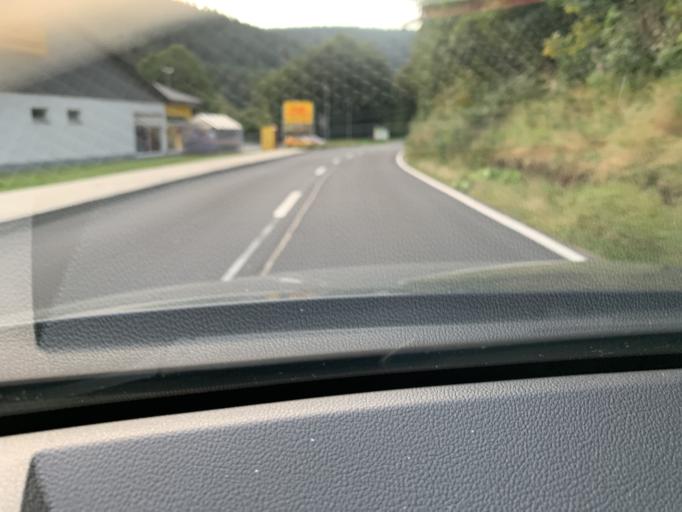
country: DE
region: Thuringia
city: Steinach
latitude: 50.4203
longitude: 11.1678
